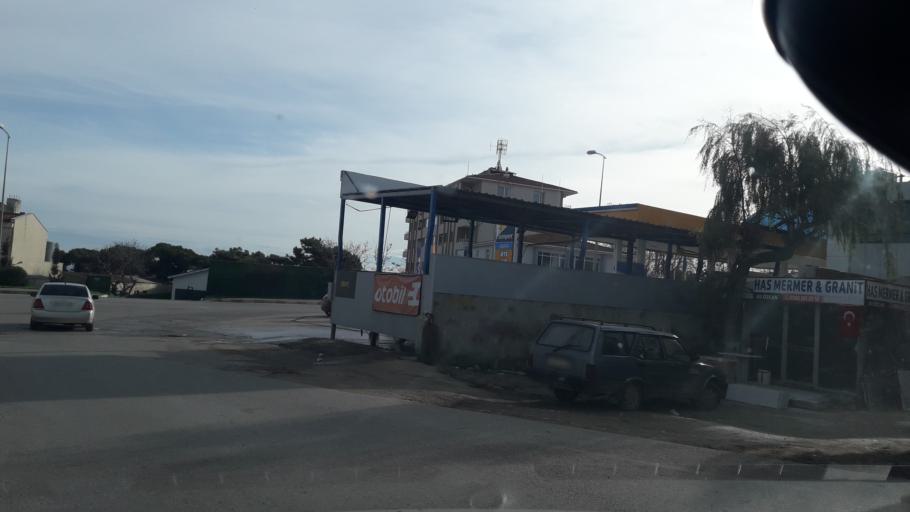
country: TR
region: Sinop
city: Sinop
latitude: 42.0244
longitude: 35.1385
